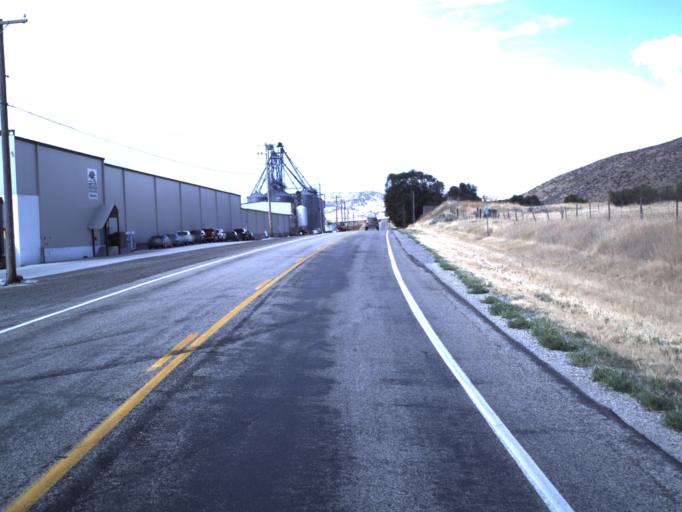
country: US
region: Utah
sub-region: Box Elder County
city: Garland
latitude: 41.7716
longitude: -112.0964
